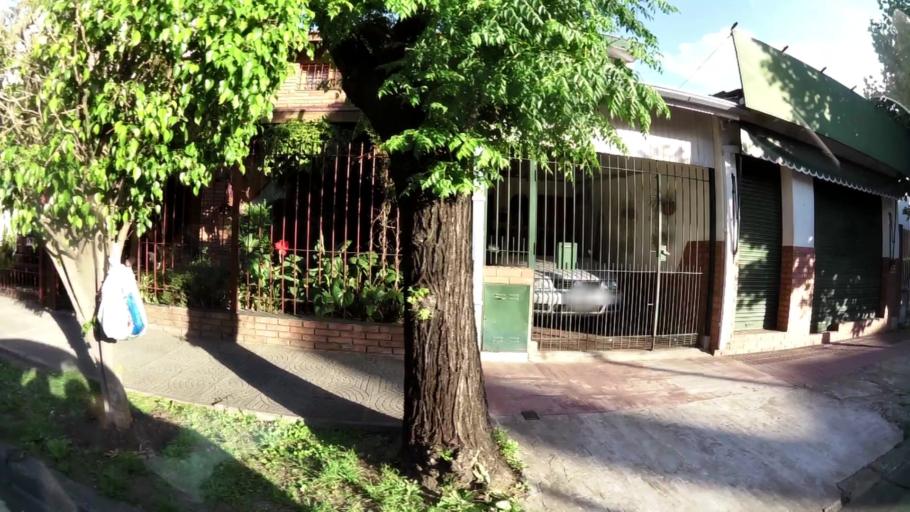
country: AR
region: Buenos Aires
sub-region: Partido de General San Martin
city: General San Martin
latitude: -34.5578
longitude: -58.5610
